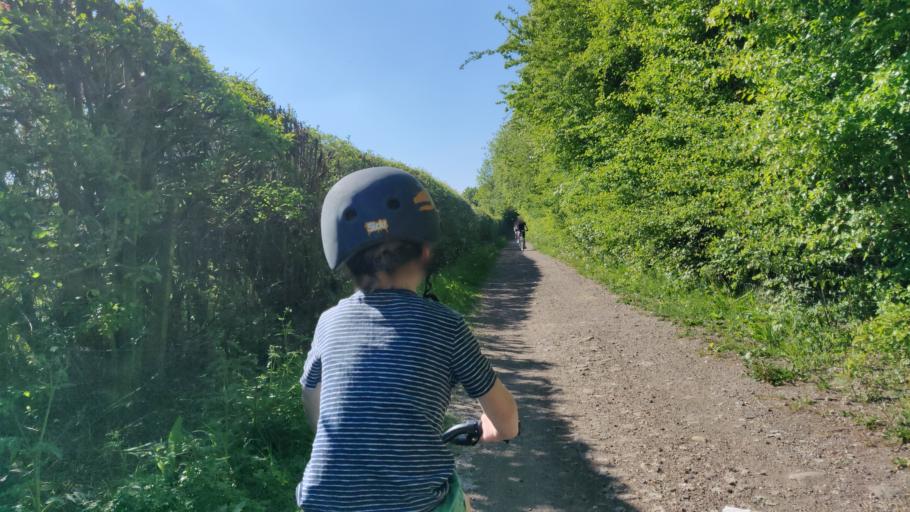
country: GB
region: England
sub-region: West Sussex
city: Southwater
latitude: 51.0630
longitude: -0.3957
